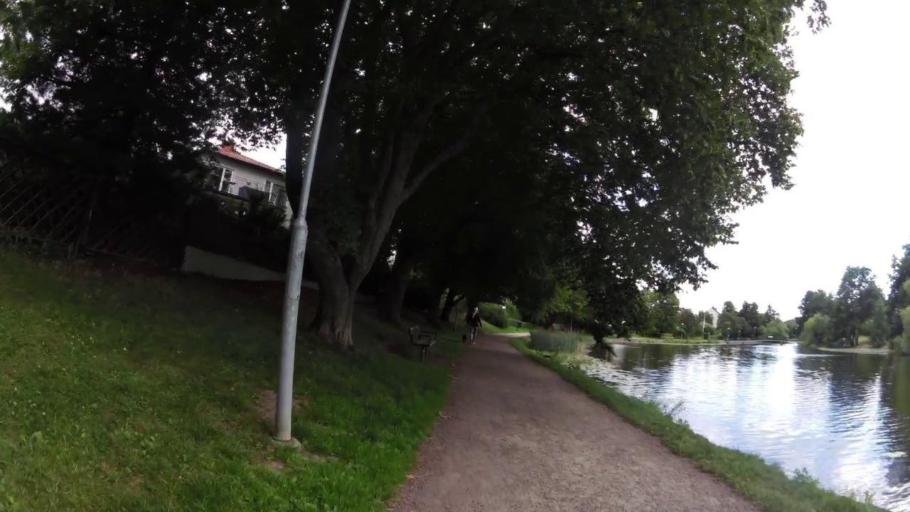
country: SE
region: OEstergoetland
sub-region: Linkopings Kommun
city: Linkoping
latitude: 58.4049
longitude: 15.6389
